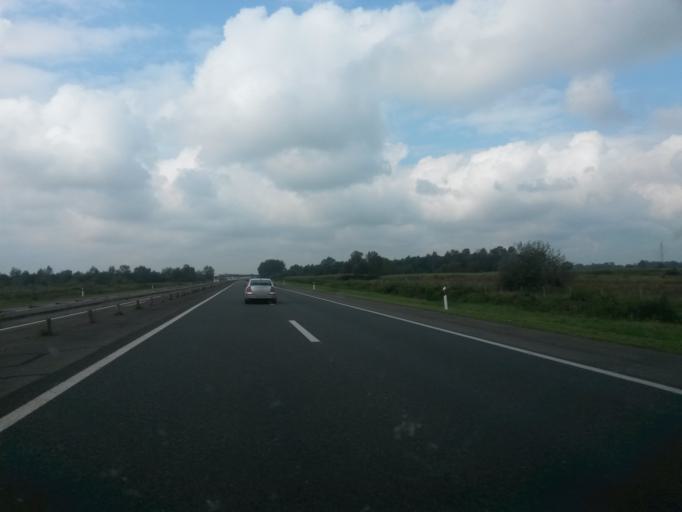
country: HR
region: Zagrebacka
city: Kriz
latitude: 45.6846
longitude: 16.4158
